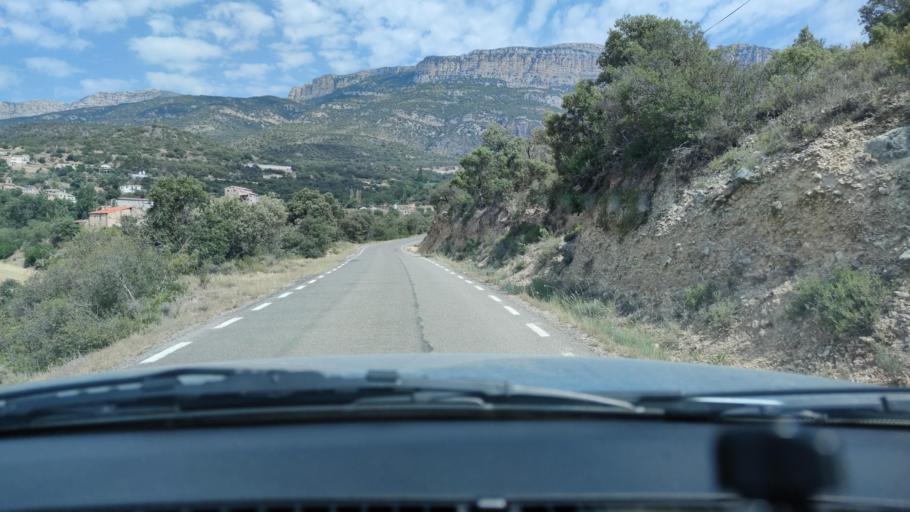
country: ES
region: Catalonia
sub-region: Provincia de Lleida
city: Ager
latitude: 42.0104
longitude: 0.8316
